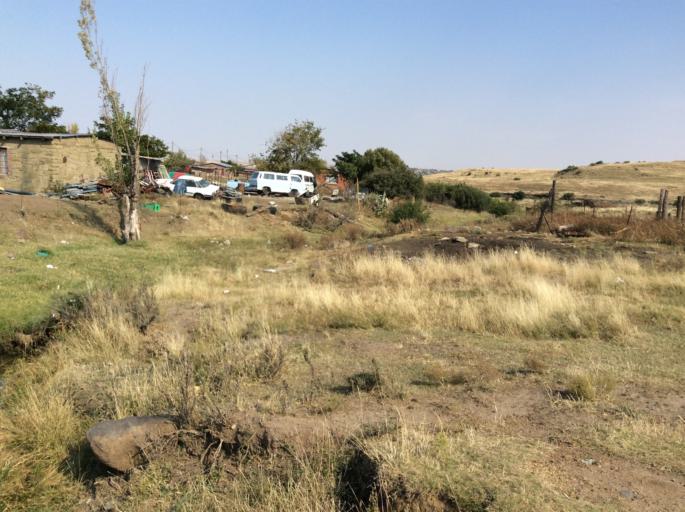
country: LS
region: Mafeteng
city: Mafeteng
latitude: -29.7153
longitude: 27.0298
